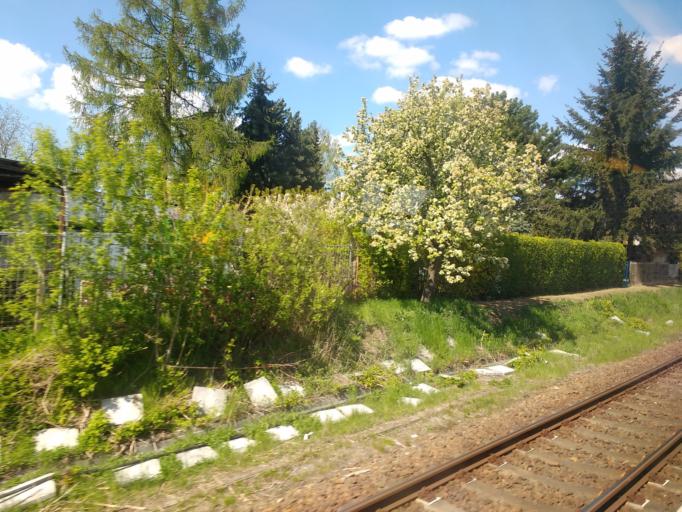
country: DE
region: Berlin
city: Altglienicke
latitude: 52.4015
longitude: 13.5489
